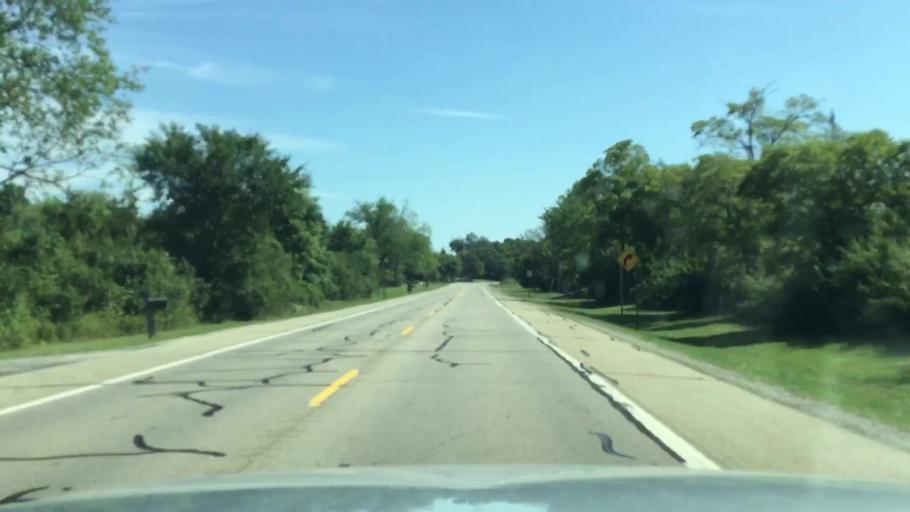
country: US
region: Michigan
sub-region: Jackson County
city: Brooklyn
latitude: 42.0611
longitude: -84.1953
